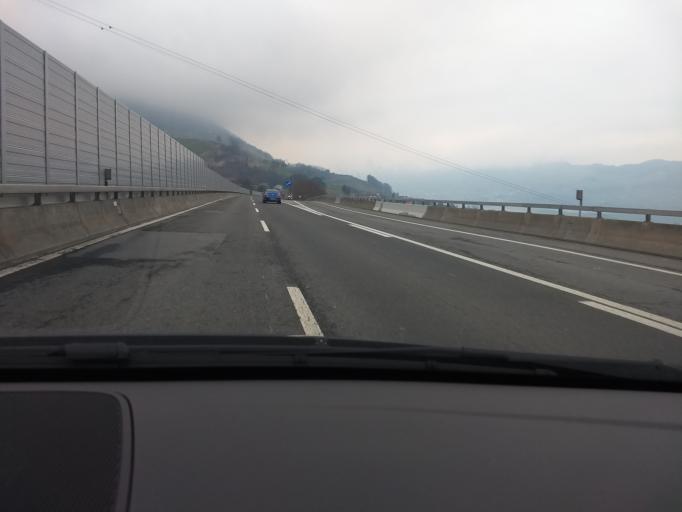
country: CH
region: Nidwalden
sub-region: Nidwalden
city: Beckenried
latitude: 46.9624
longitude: 8.4767
